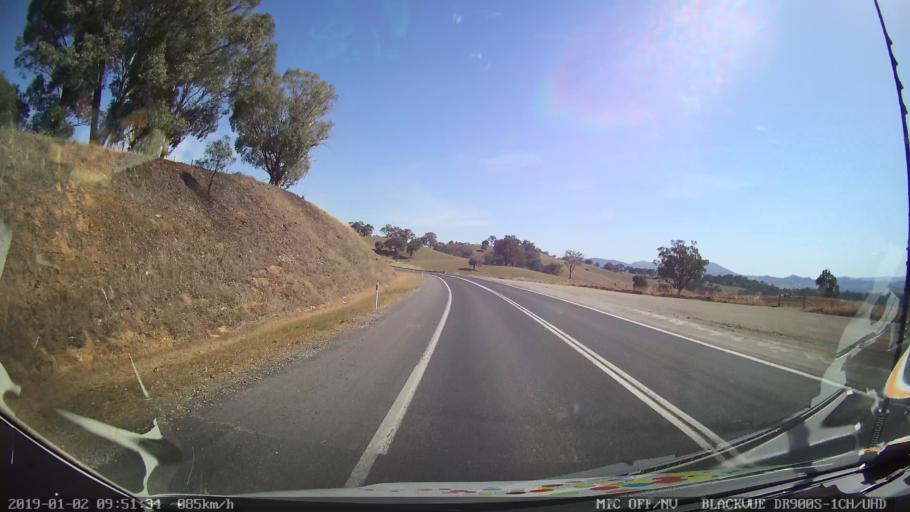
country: AU
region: New South Wales
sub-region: Tumut Shire
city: Tumut
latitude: -35.2715
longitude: 148.2113
